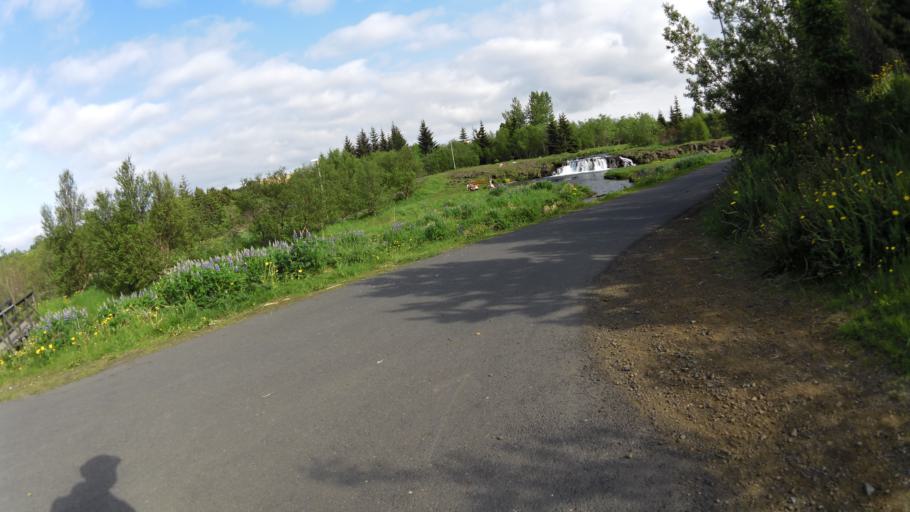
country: IS
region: Capital Region
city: Reykjavik
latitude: 64.1214
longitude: -21.8466
